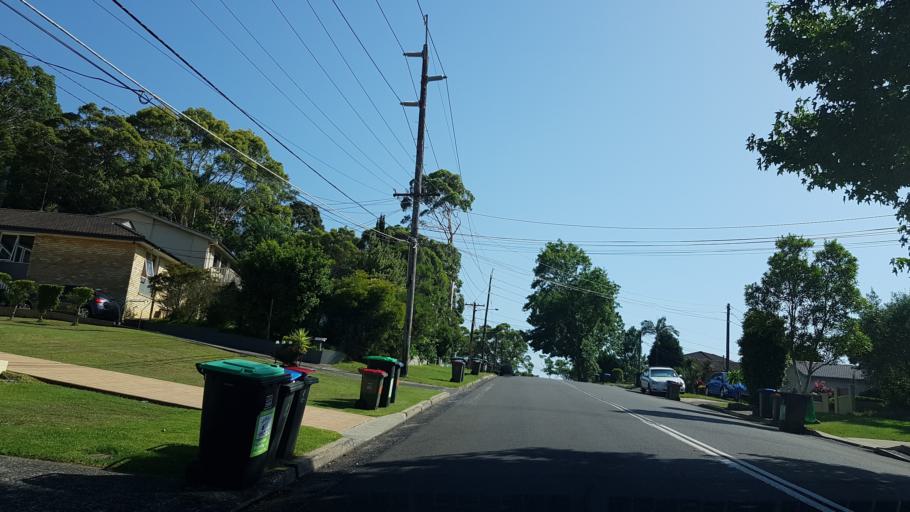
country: AU
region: New South Wales
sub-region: Warringah
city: Narraweena
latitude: -33.7370
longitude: 151.2710
